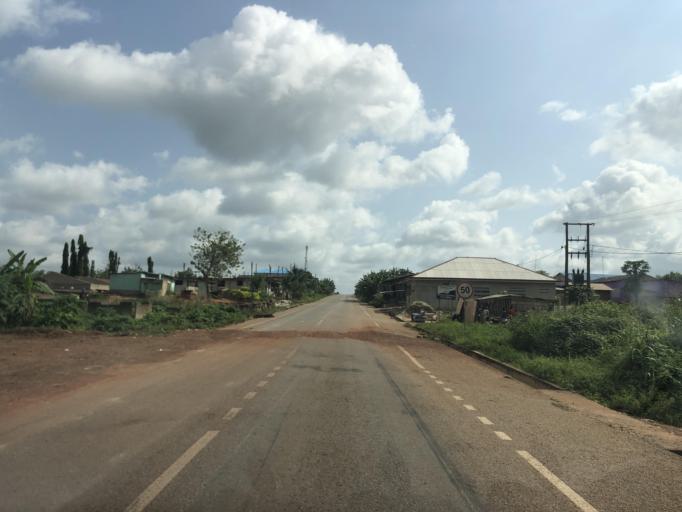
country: GH
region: Central
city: Cape Coast
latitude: 5.2059
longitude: -1.3207
